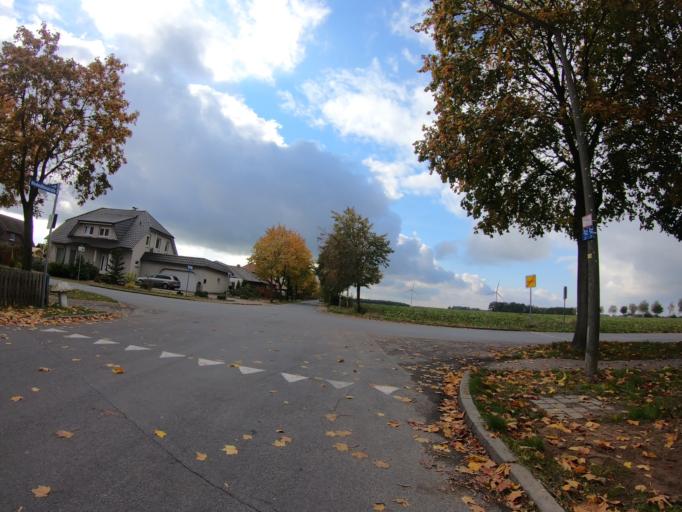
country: DE
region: Lower Saxony
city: Wahrenholz
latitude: 52.6079
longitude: 10.5948
